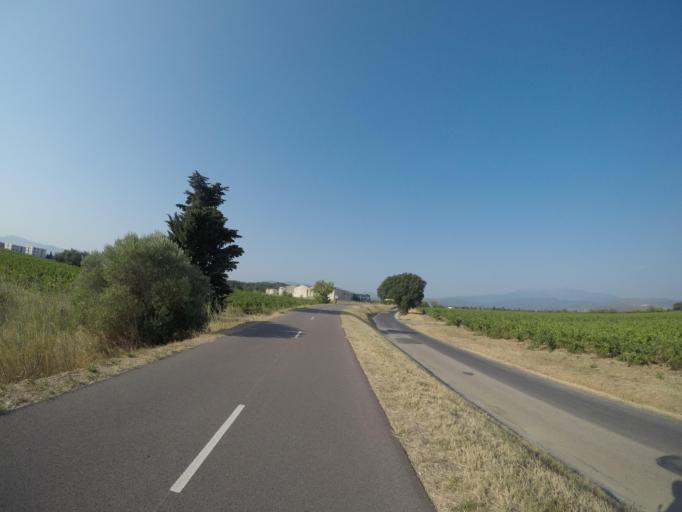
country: FR
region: Languedoc-Roussillon
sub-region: Departement des Pyrenees-Orientales
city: Ponteilla
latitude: 42.6307
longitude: 2.8058
